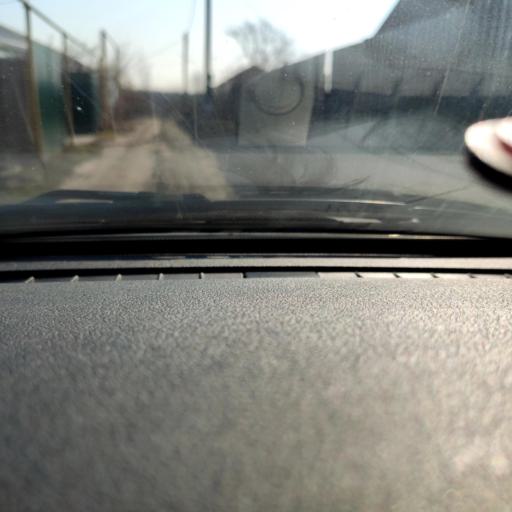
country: RU
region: Voronezj
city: Novaya Usman'
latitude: 51.6432
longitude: 39.4218
